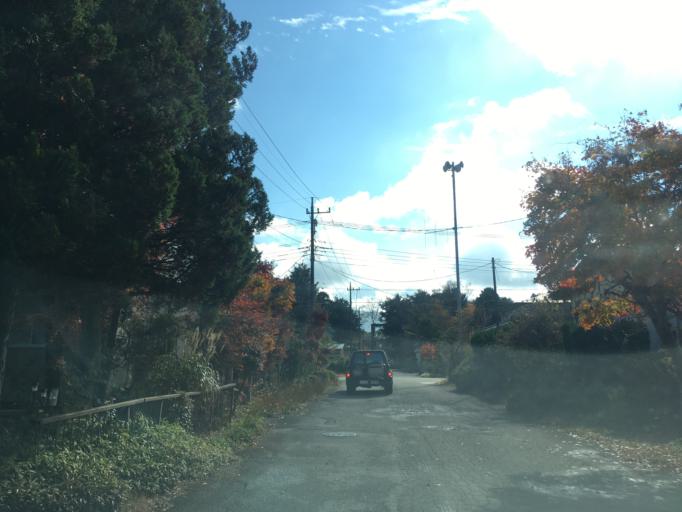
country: JP
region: Yamanashi
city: Fujikawaguchiko
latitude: 35.4798
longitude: 138.6124
